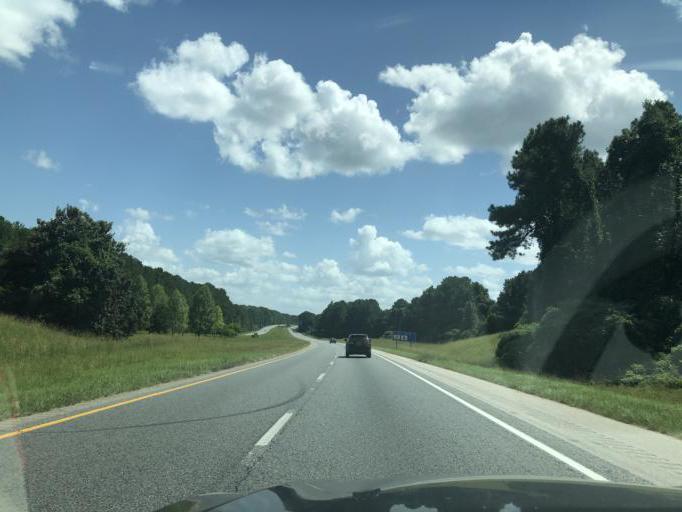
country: US
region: Georgia
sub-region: Troup County
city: La Grange
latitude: 33.0296
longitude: -84.9541
